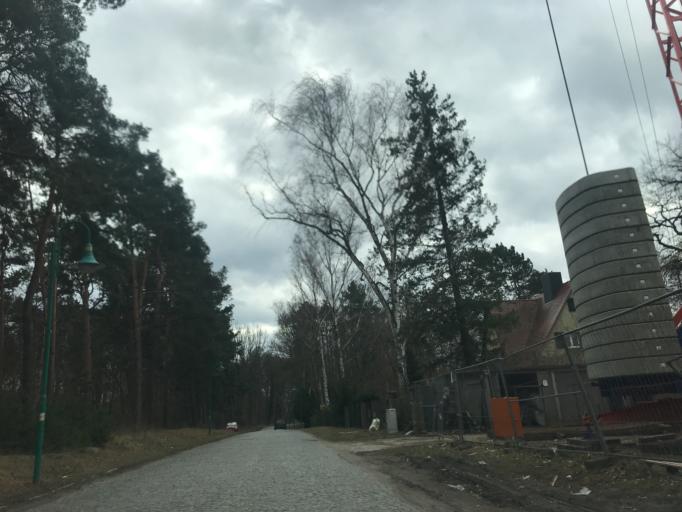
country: DE
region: Brandenburg
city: Zossen
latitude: 52.1509
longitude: 13.4755
